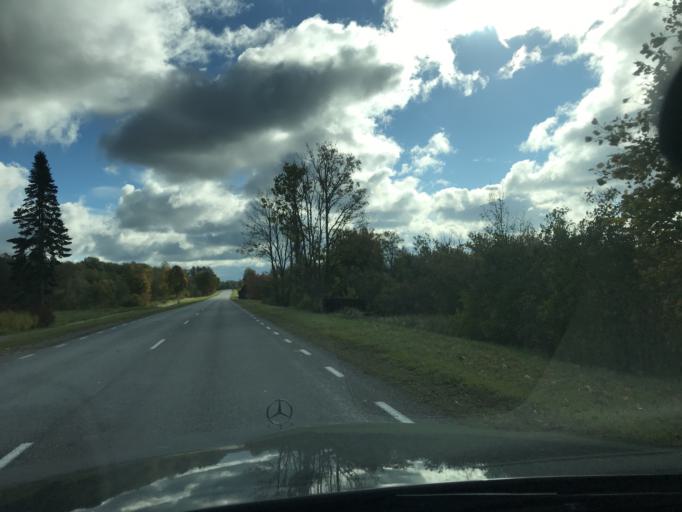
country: EE
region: Vorumaa
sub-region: Antsla vald
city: Vana-Antsla
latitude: 57.9479
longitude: 26.2929
